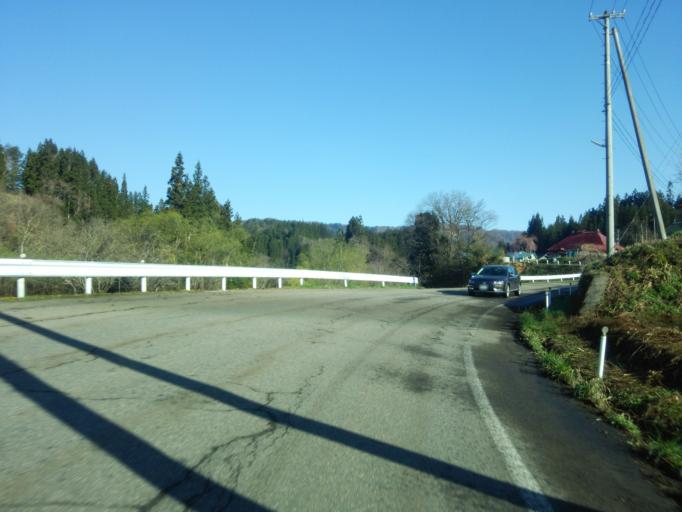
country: JP
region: Fukushima
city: Kitakata
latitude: 37.7049
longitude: 139.7849
